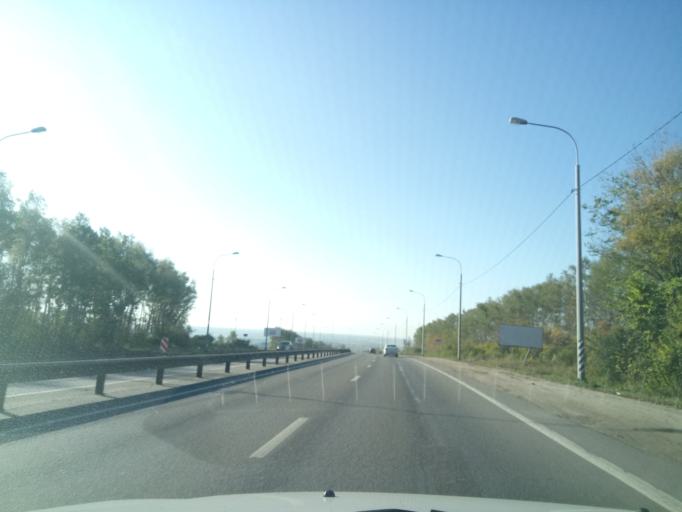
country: RU
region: Nizjnij Novgorod
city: Nizhniy Novgorod
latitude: 56.2054
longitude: 43.9262
